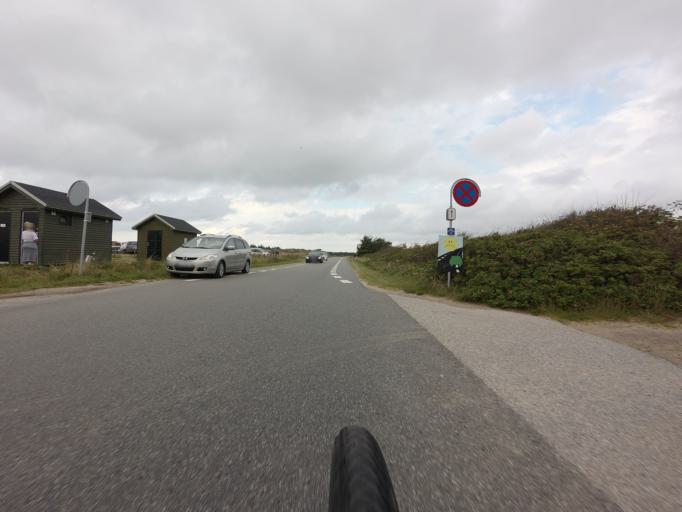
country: DK
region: North Denmark
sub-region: Hjorring Kommune
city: Hjorring
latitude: 57.4513
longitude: 9.7957
